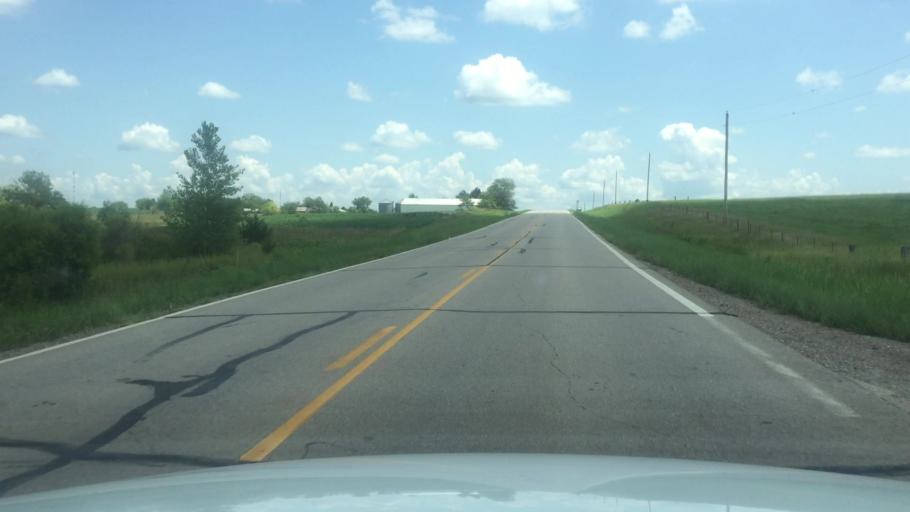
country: US
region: Kansas
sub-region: Brown County
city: Horton
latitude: 39.6674
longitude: -95.6203
